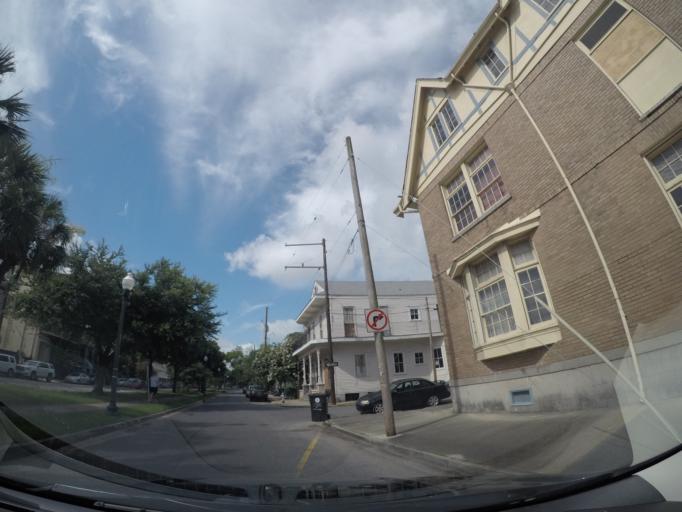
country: US
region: Louisiana
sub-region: Orleans Parish
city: New Orleans
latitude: 29.9395
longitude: -90.0724
